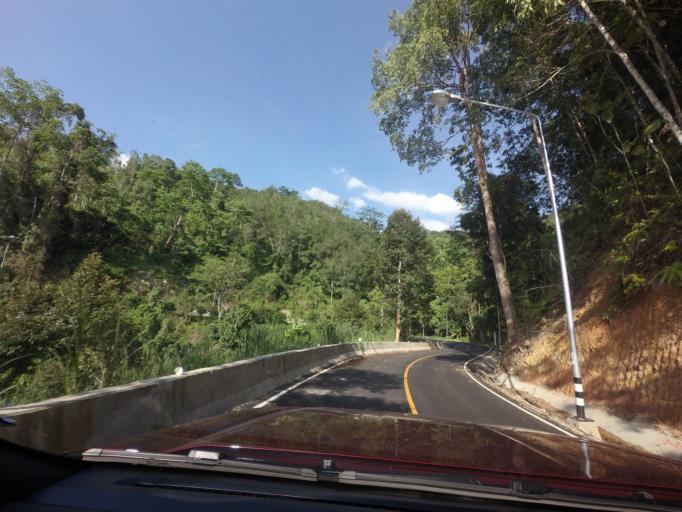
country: TH
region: Yala
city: Than To
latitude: 6.1311
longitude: 101.2986
